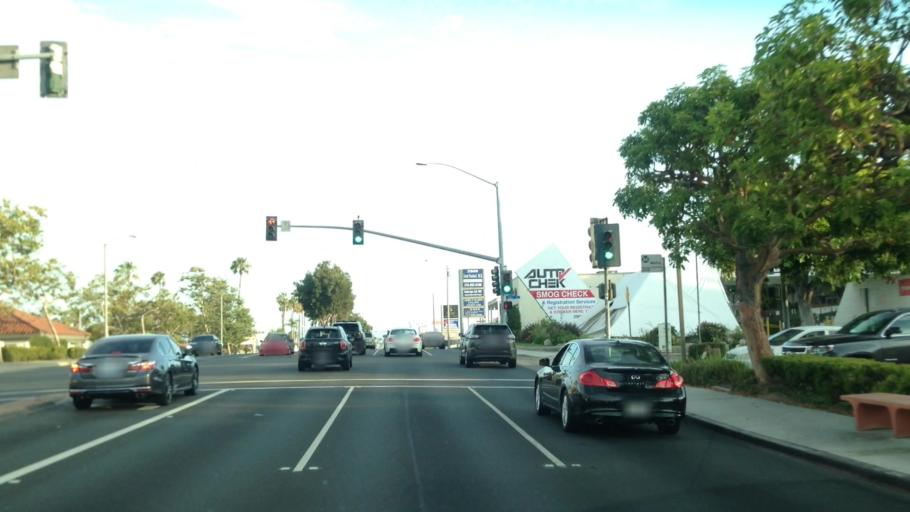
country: US
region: California
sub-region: Los Angeles County
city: Manhattan Beach
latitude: 33.8976
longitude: -118.3961
